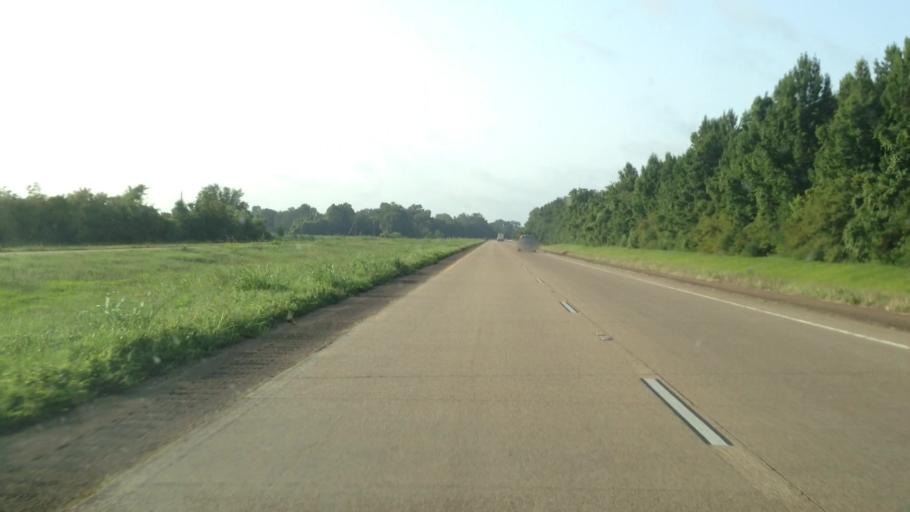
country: US
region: Louisiana
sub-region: Rapides Parish
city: Woodworth
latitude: 31.1378
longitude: -92.4497
